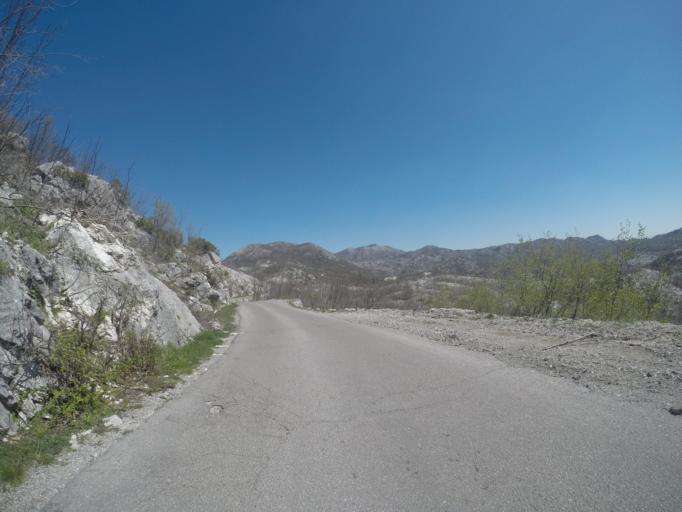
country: ME
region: Cetinje
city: Cetinje
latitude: 42.4379
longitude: 18.8710
